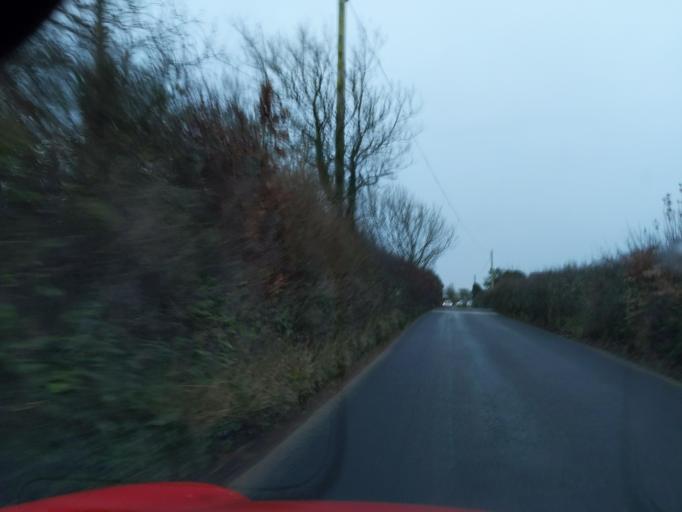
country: GB
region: England
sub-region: Devon
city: Wembury
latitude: 50.3307
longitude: -4.0638
